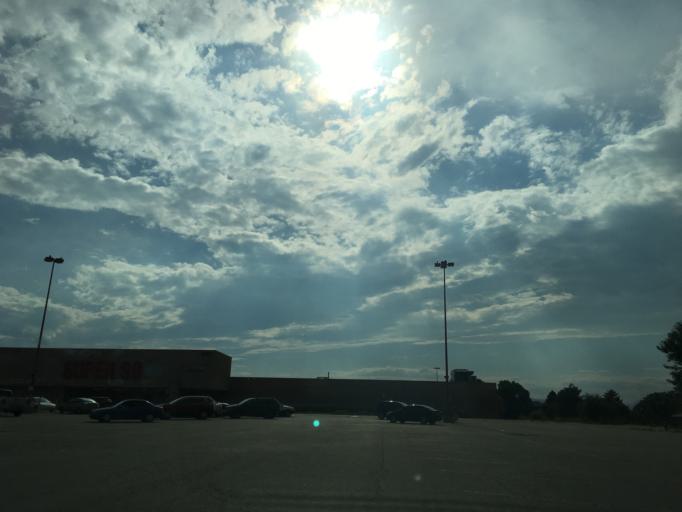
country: US
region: Colorado
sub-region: Jefferson County
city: Lakewood
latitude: 39.6783
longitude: -105.0550
